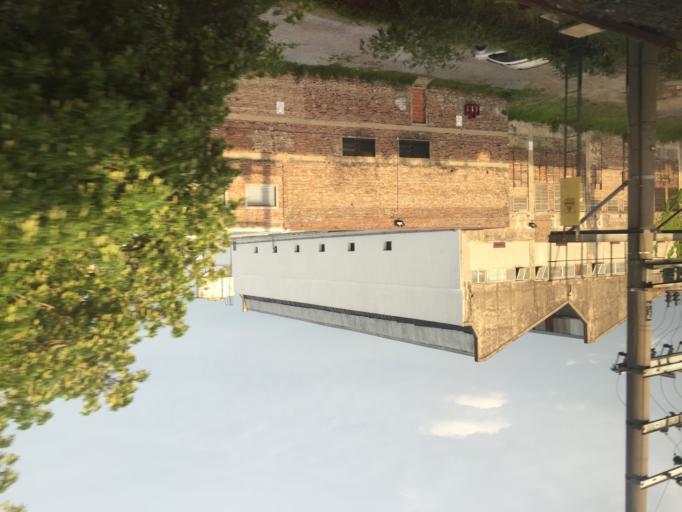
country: AR
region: Buenos Aires
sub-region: Partido de Avellaneda
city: Avellaneda
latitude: -34.6560
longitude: -58.3782
